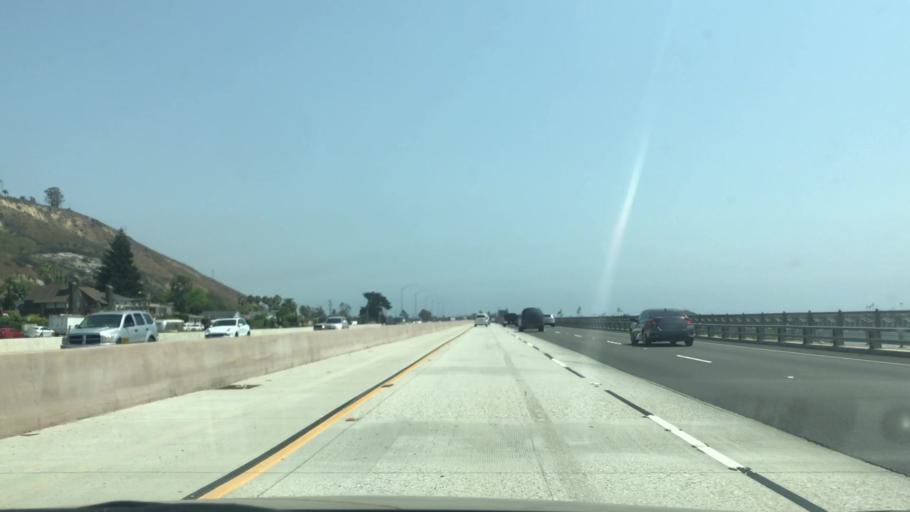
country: US
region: California
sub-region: Santa Barbara County
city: Carpinteria
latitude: 34.3643
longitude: -119.4512
